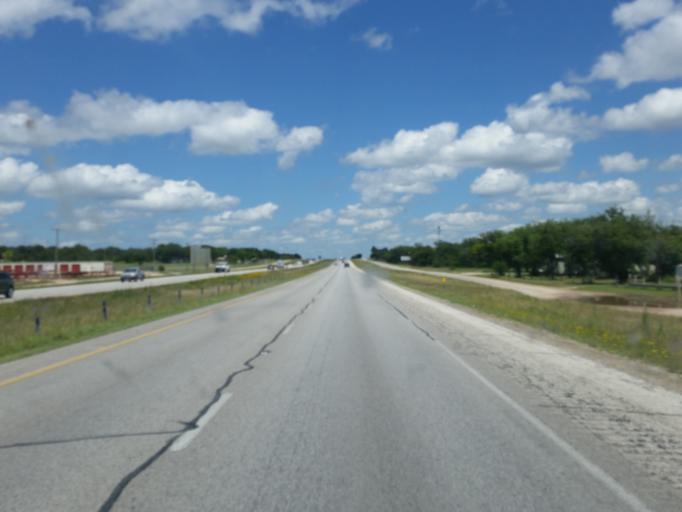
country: US
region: Texas
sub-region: Callahan County
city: Clyde
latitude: 32.4095
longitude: -99.4712
